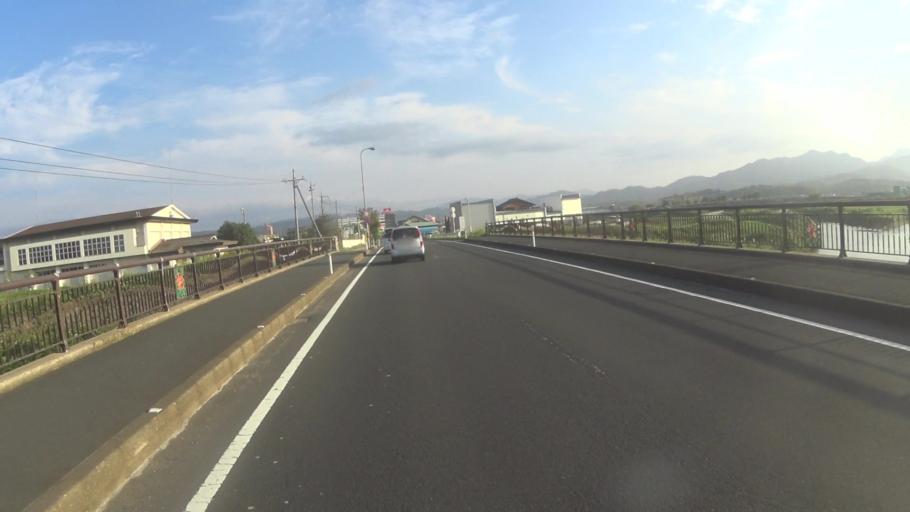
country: JP
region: Kyoto
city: Miyazu
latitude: 35.6148
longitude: 135.0781
